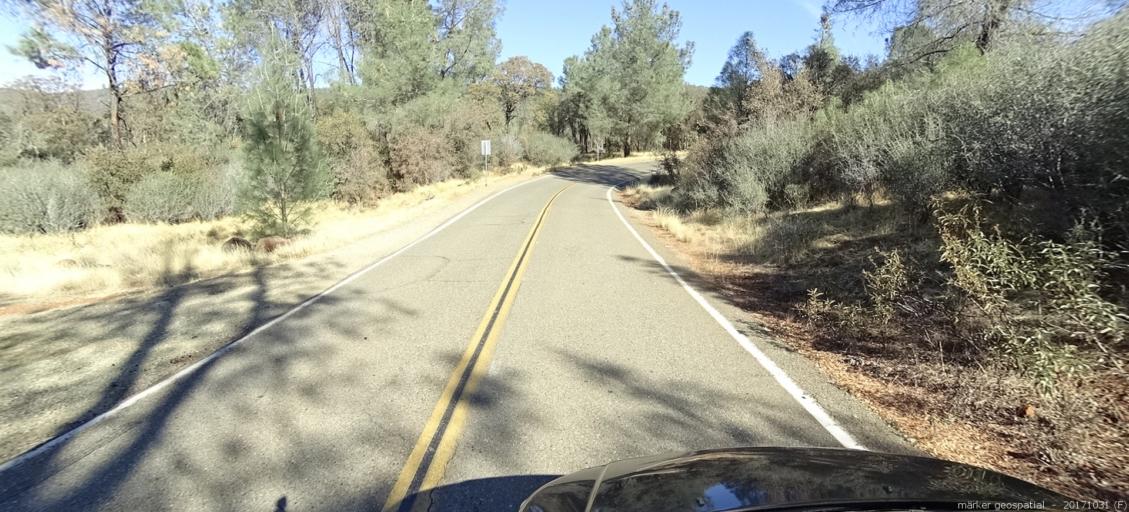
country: US
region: California
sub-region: Shasta County
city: Shingletown
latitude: 40.4493
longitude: -121.8900
